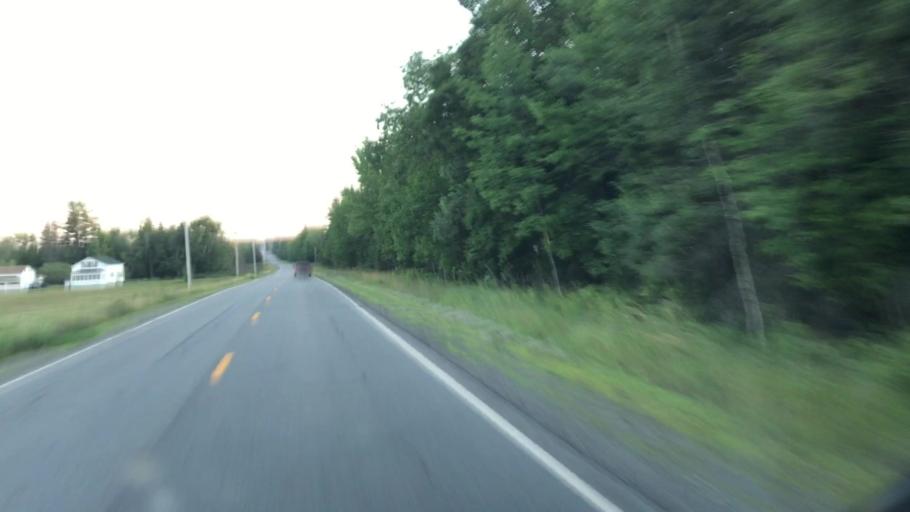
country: US
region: Maine
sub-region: Penobscot County
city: Medway
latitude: 45.6124
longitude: -68.3048
